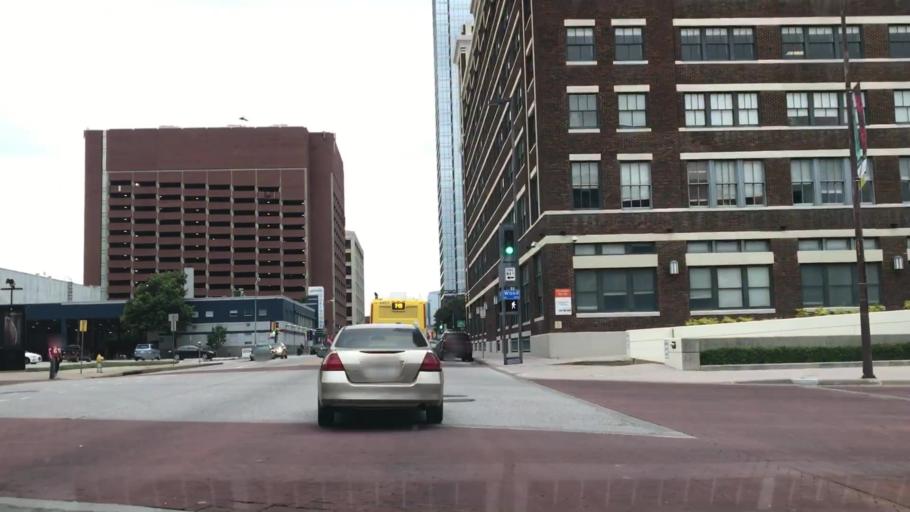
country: US
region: Texas
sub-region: Dallas County
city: Dallas
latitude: 32.7771
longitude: -96.8035
